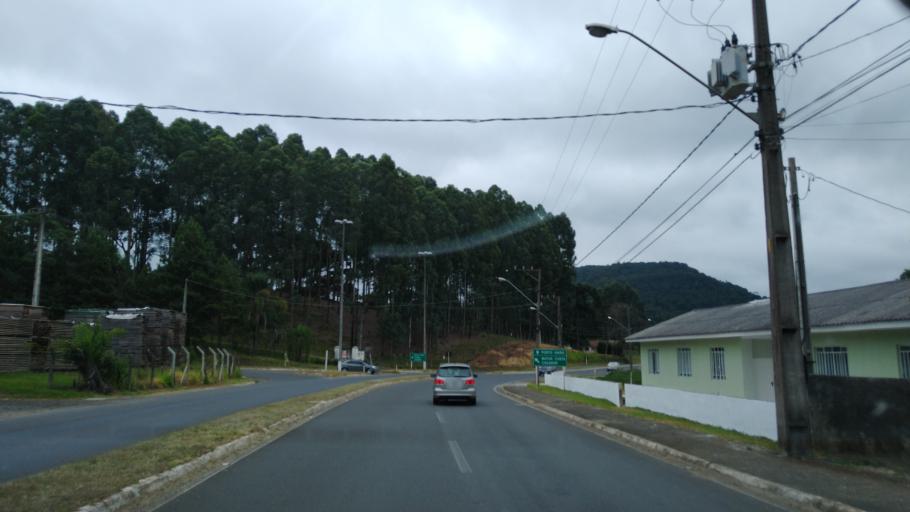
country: BR
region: Santa Catarina
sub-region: Porto Uniao
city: Porto Uniao
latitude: -26.2816
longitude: -51.0486
